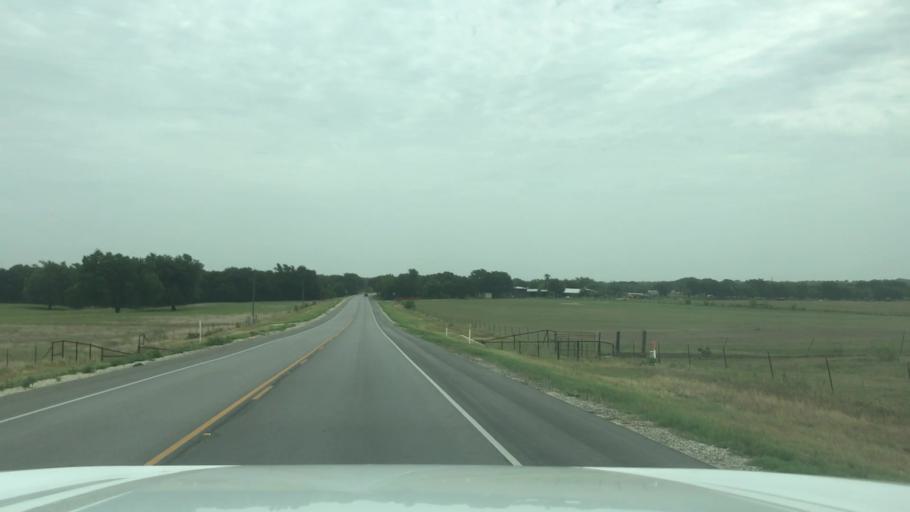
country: US
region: Texas
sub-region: Erath County
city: Dublin
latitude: 32.0870
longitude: -98.3091
